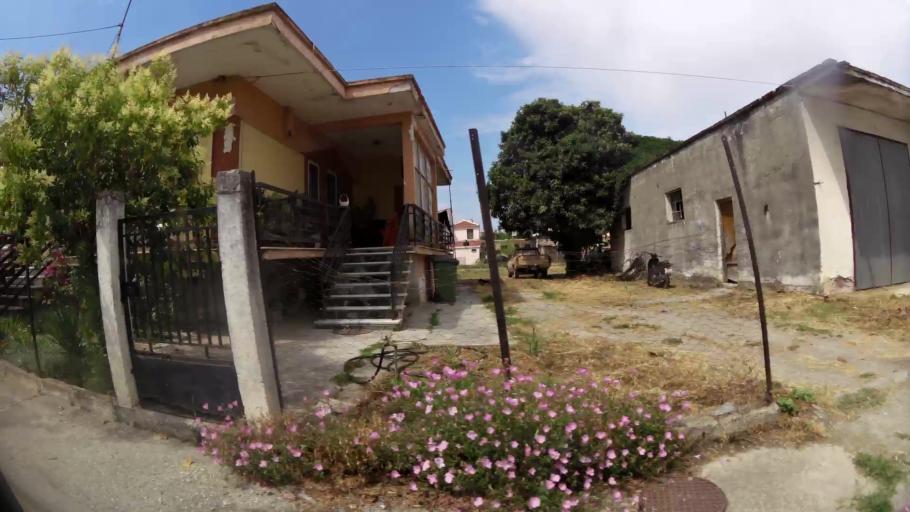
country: GR
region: Central Macedonia
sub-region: Nomos Pierias
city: Korinos
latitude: 40.3144
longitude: 22.5807
